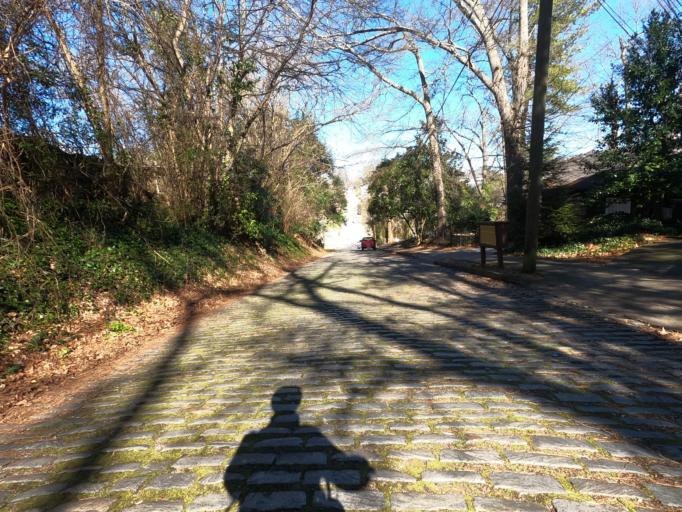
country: US
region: Georgia
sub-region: Clarke County
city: Athens
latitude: 33.9554
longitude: -83.3825
